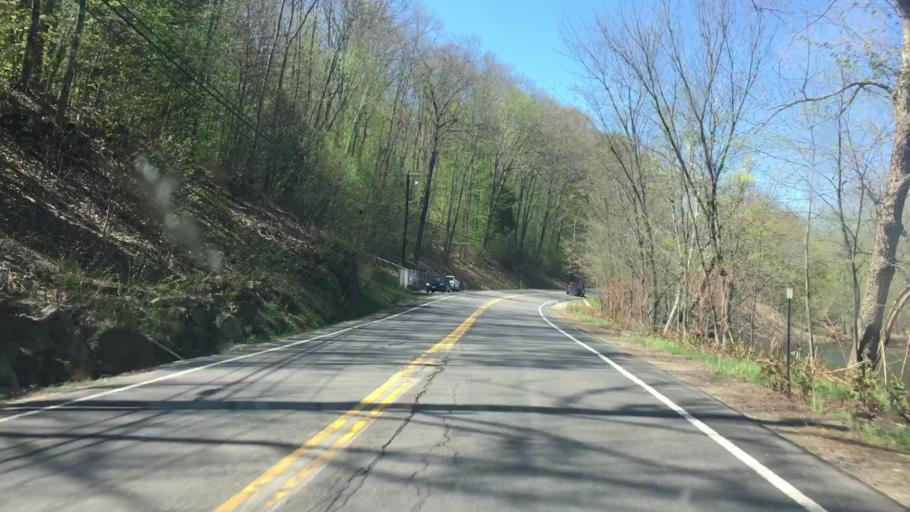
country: US
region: New Hampshire
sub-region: Grafton County
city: Plymouth
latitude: 43.7435
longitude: -71.6796
